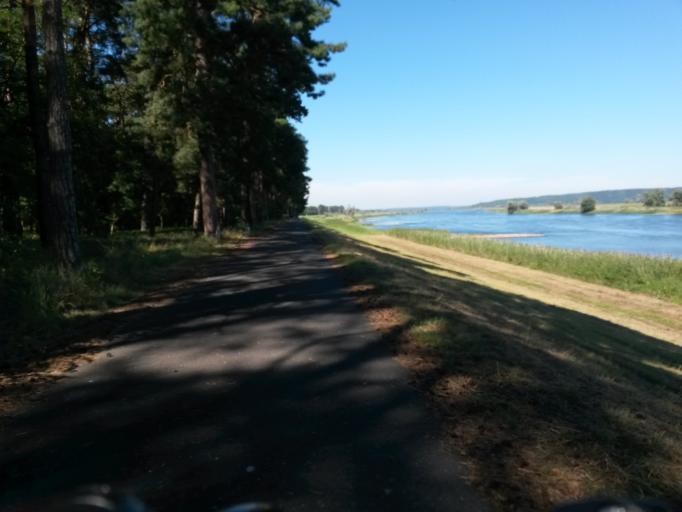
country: PL
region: West Pomeranian Voivodeship
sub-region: Powiat gryfinski
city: Cedynia
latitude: 52.8936
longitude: 14.1549
